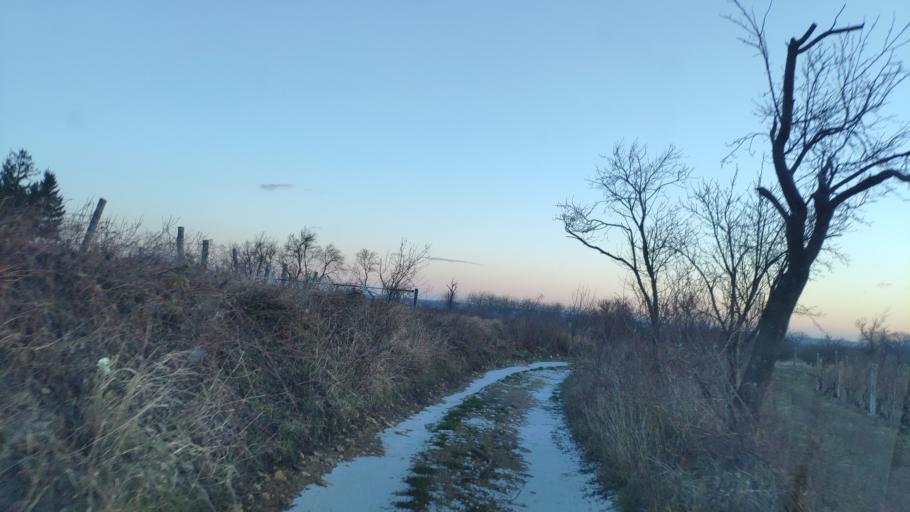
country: HU
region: Borsod-Abauj-Zemplen
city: Olaszliszka
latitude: 48.2736
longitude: 21.3981
